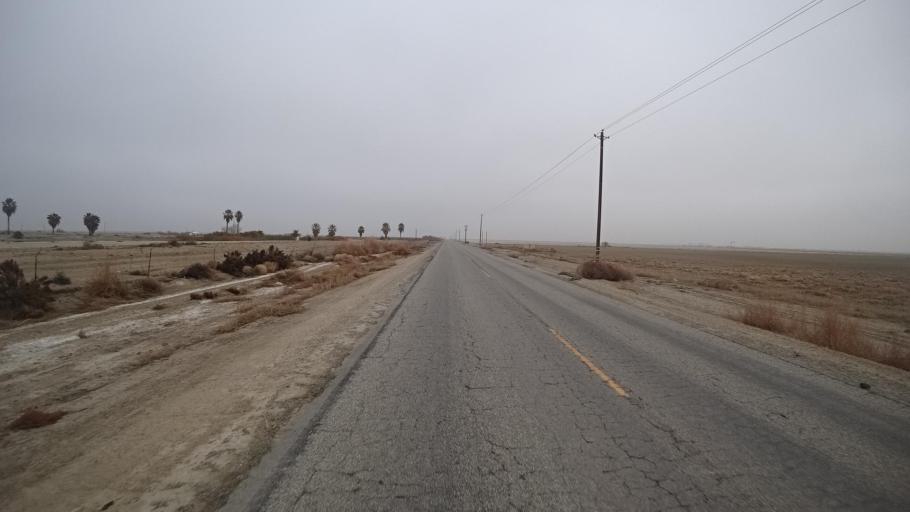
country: US
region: California
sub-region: Kern County
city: Maricopa
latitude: 35.1519
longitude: -119.2280
